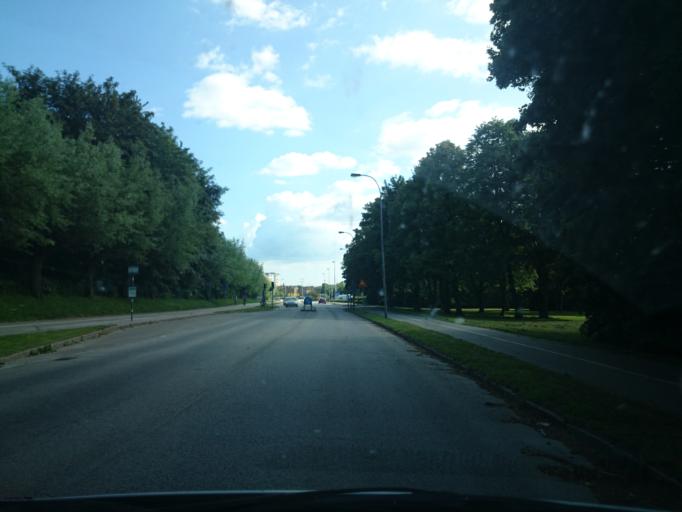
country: SE
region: Skane
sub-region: Lunds Kommun
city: Lund
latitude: 55.7152
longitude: 13.1805
